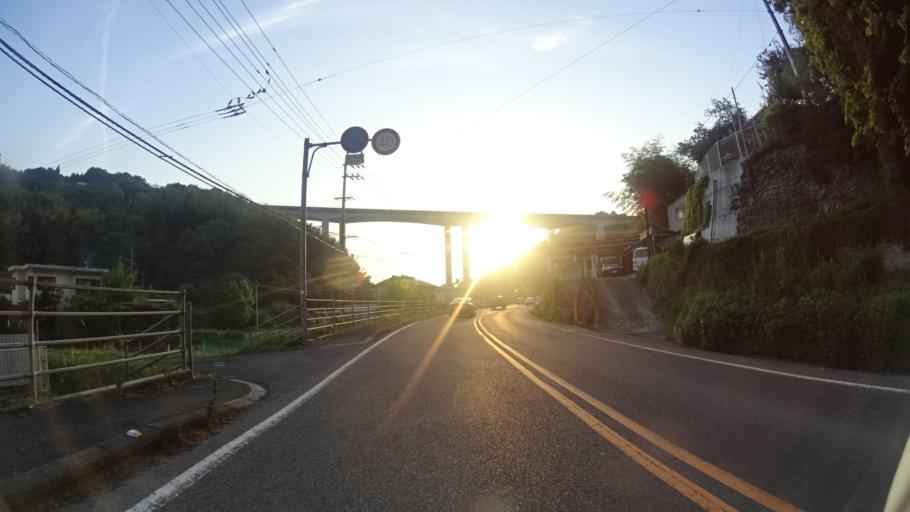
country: JP
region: Ehime
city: Kawanoecho
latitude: 33.9919
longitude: 133.6229
